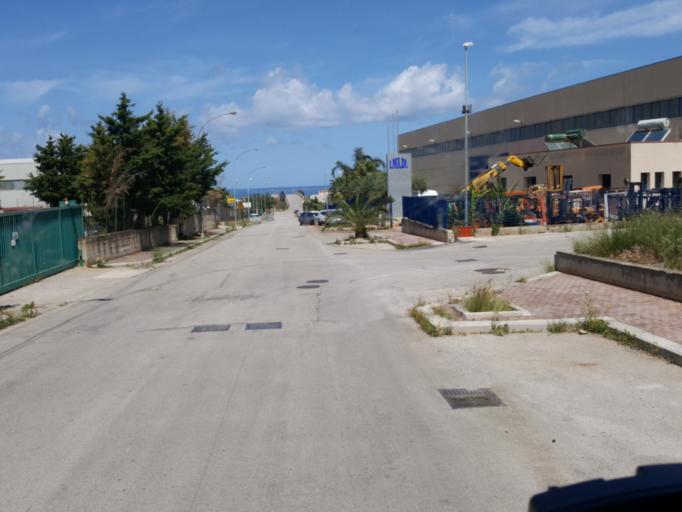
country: IT
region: Sicily
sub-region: Palermo
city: Carini
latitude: 38.1549
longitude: 13.2109
